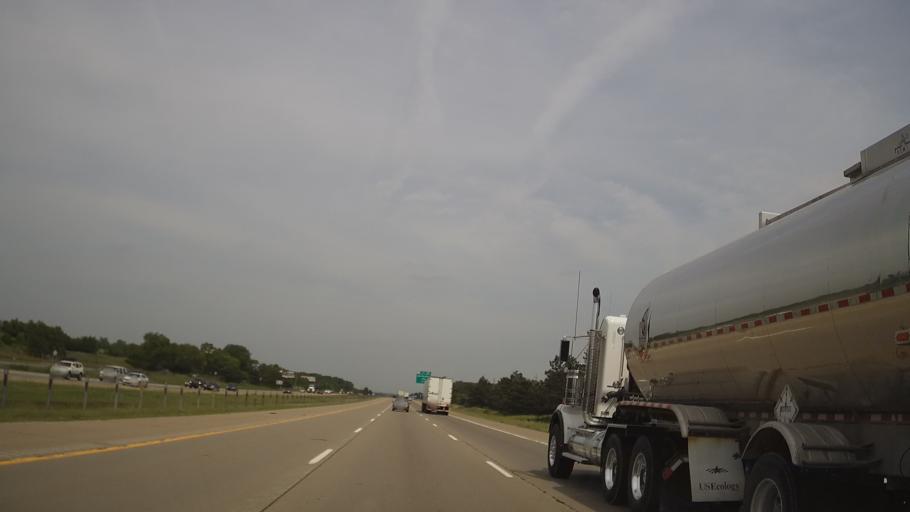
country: US
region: Michigan
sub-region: Wayne County
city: Belleville
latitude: 42.2189
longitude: -83.5154
